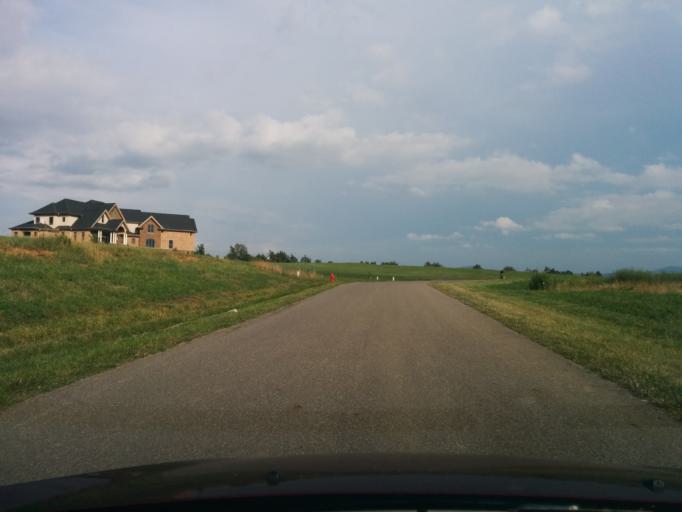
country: US
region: Virginia
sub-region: Rockbridge County
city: East Lexington
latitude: 37.7939
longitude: -79.4048
